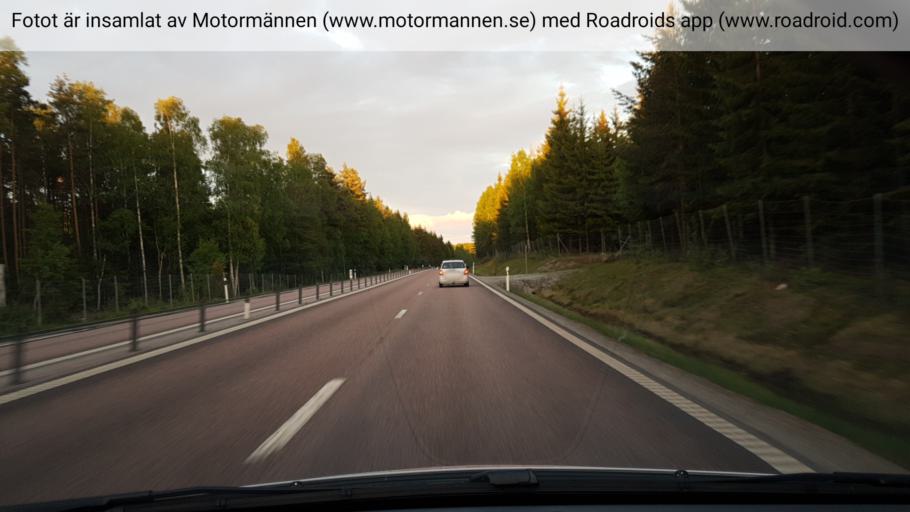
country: SE
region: Vaestmanland
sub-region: Fagersta Kommun
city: Fagersta
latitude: 59.9401
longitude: 15.8987
